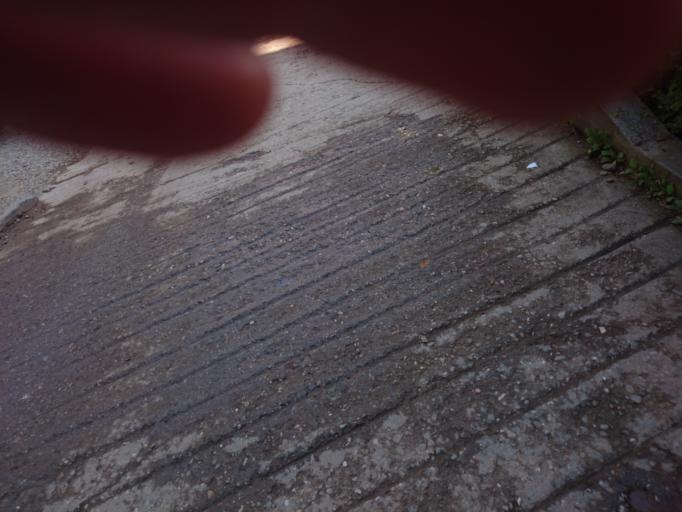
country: AL
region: Diber
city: Peshkopi
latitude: 41.6853
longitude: 20.4289
